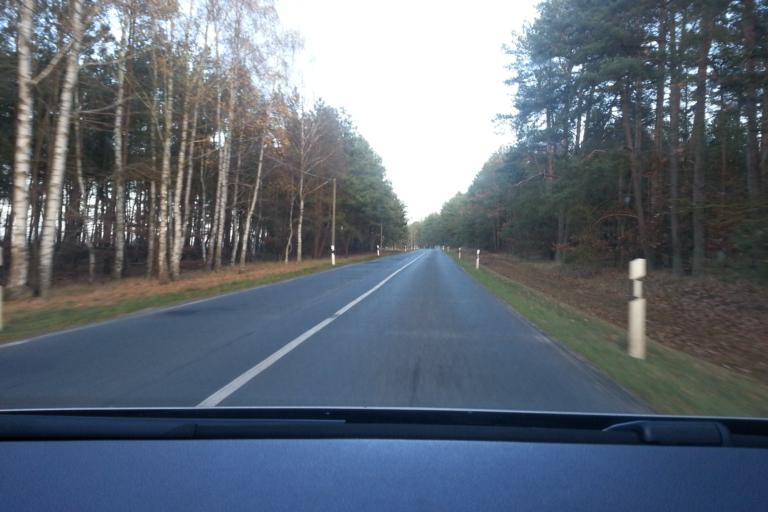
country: DE
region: Mecklenburg-Vorpommern
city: Ferdinandshof
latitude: 53.6203
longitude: 13.7875
